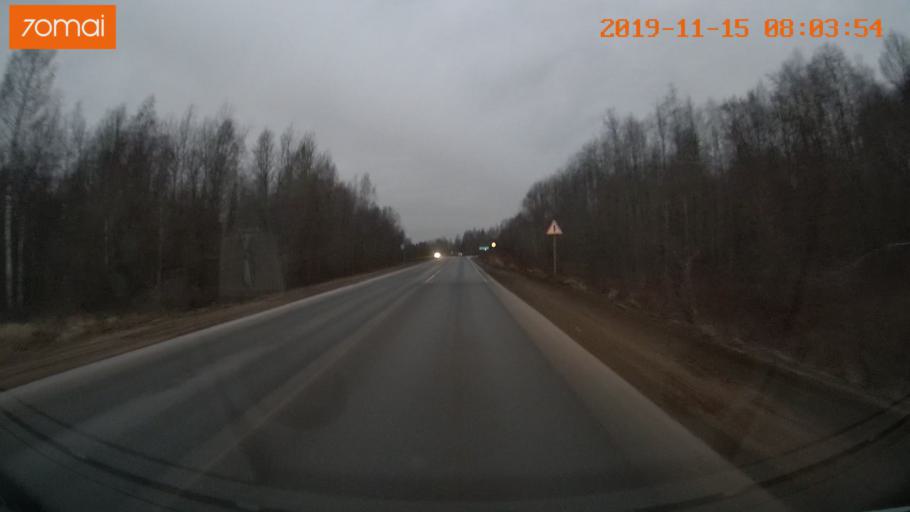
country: RU
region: Vologda
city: Cherepovets
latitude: 59.0028
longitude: 38.0834
